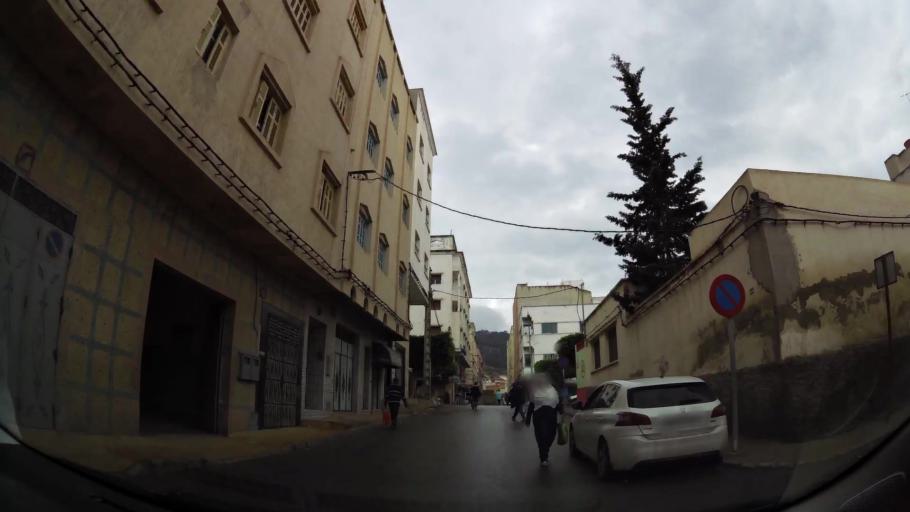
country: MA
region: Oriental
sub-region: Nador
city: Nador
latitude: 35.1527
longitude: -3.0058
